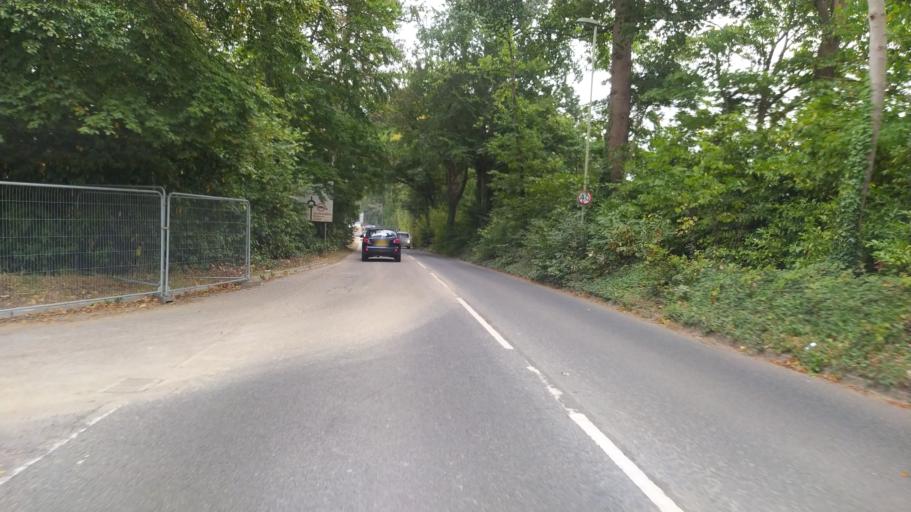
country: GB
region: England
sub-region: Hampshire
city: West End
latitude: 50.9159
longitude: -1.3294
